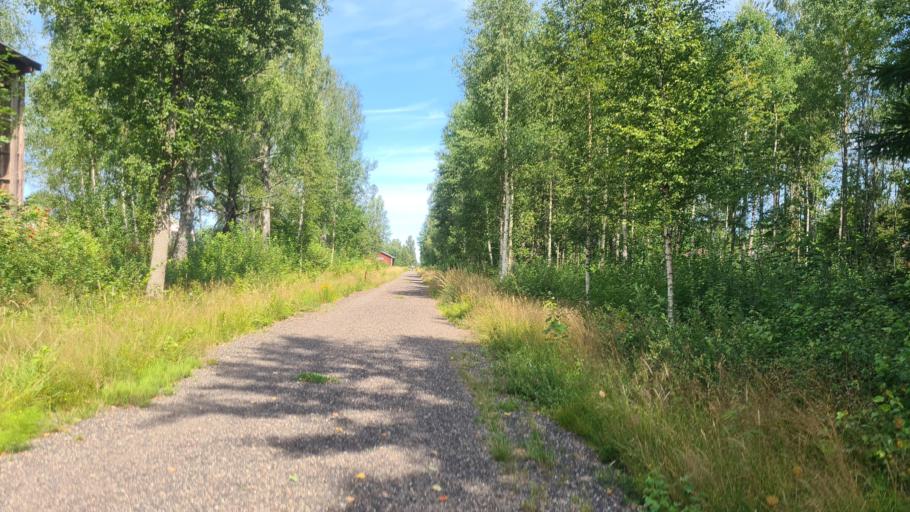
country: SE
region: Kronoberg
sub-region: Ljungby Kommun
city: Lagan
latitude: 56.9687
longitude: 13.9517
